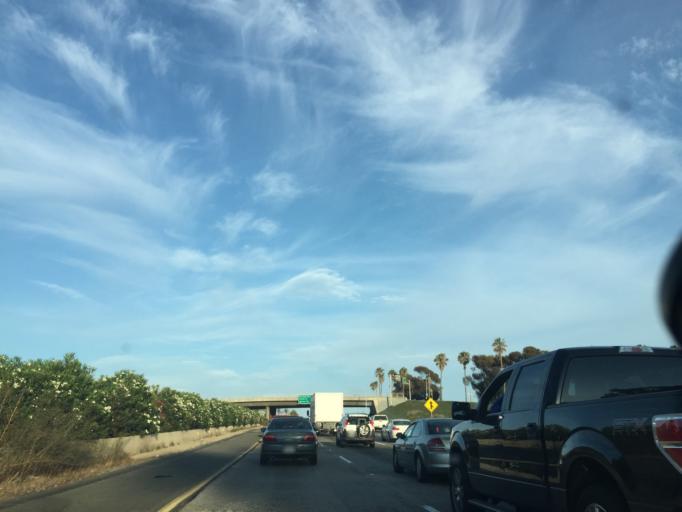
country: US
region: California
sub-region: San Diego County
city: Oceanside
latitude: 33.2009
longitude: -117.3742
